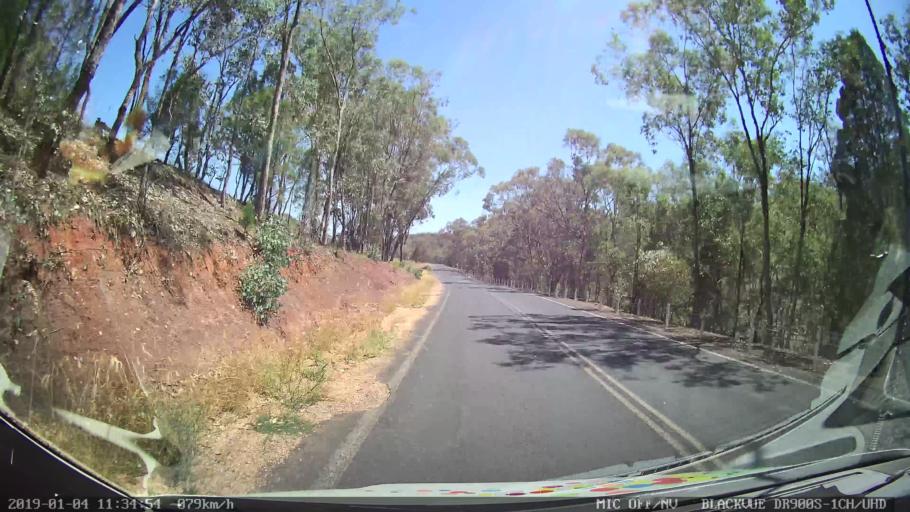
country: AU
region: New South Wales
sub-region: Cabonne
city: Molong
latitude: -33.0617
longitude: 148.8247
